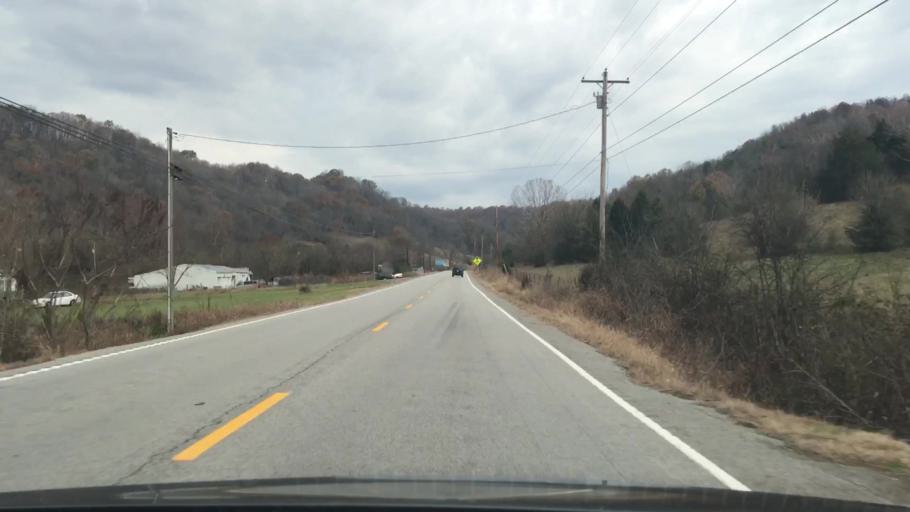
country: US
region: Tennessee
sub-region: Macon County
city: Lafayette
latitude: 36.4810
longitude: -86.0466
